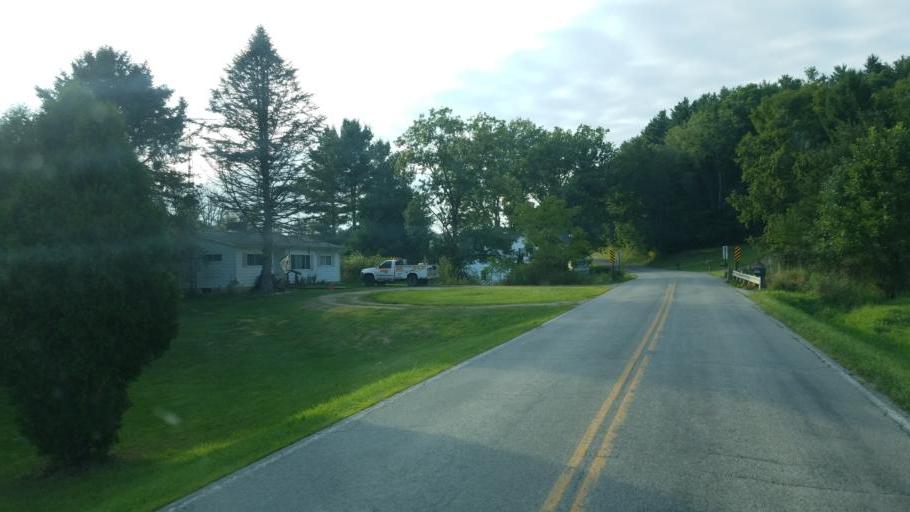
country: US
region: Ohio
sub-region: Sandusky County
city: Bellville
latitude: 40.6612
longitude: -82.4857
